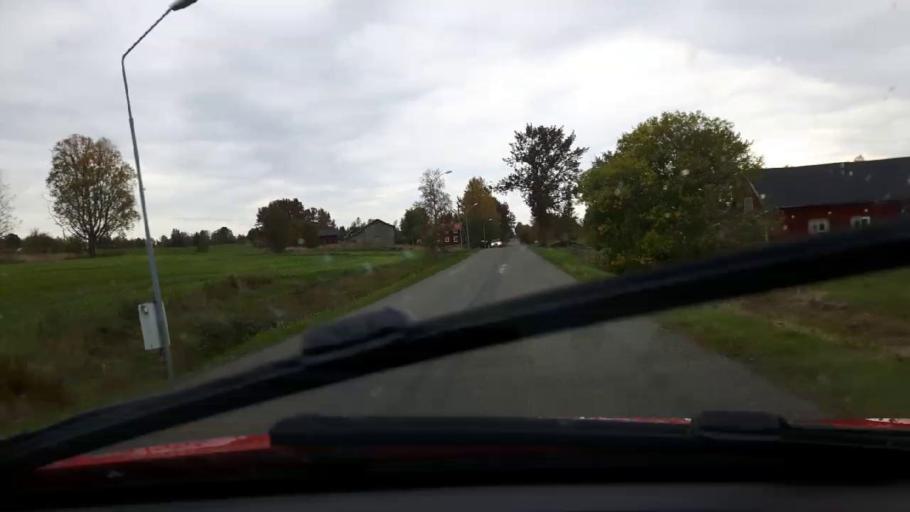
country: SE
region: Jaemtland
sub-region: Bergs Kommun
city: Hoverberg
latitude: 62.9585
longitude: 14.4902
